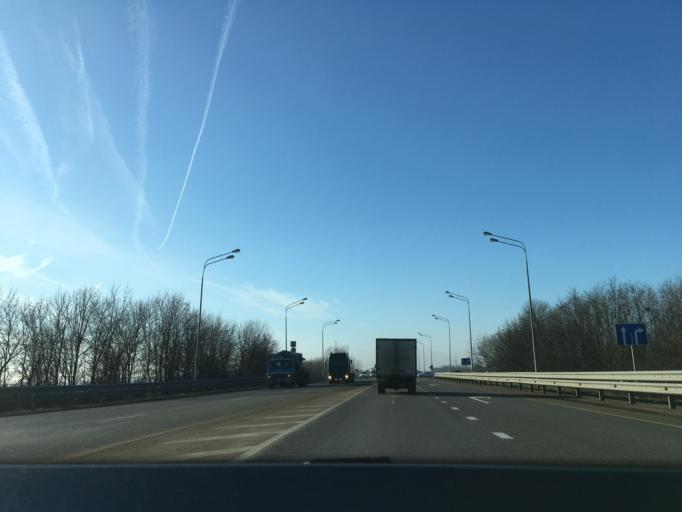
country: RU
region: Krasnodarskiy
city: Agronom
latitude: 45.1740
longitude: 39.1008
